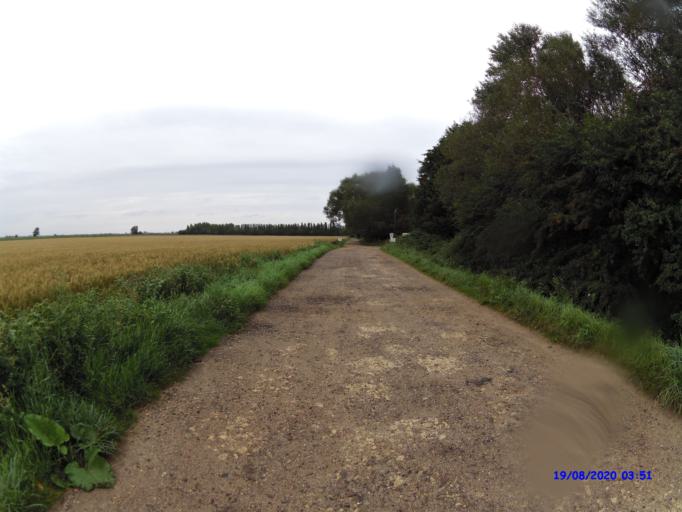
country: GB
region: England
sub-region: Cambridgeshire
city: Ramsey
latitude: 52.4646
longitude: -0.1110
